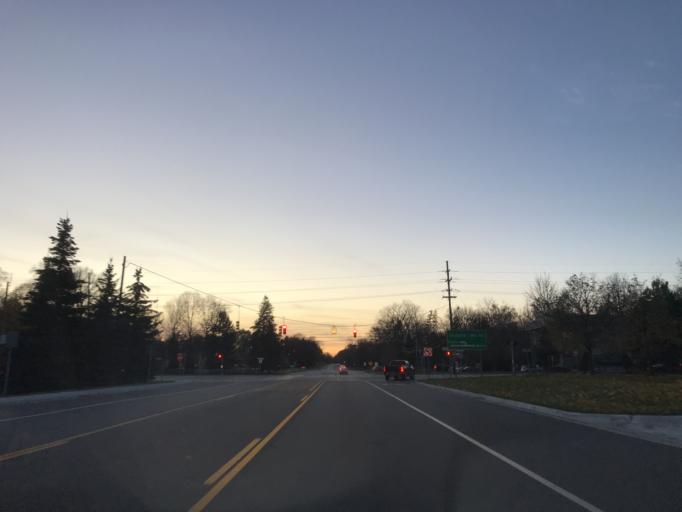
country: US
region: Michigan
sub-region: Oakland County
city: Farmington Hills
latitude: 42.4848
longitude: -83.3568
